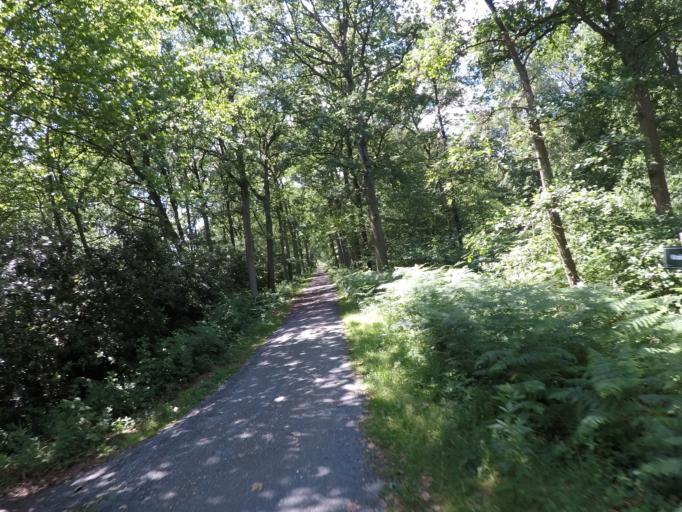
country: BE
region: Flanders
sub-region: Provincie Antwerpen
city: Vosselaar
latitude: 51.2887
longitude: 4.8873
